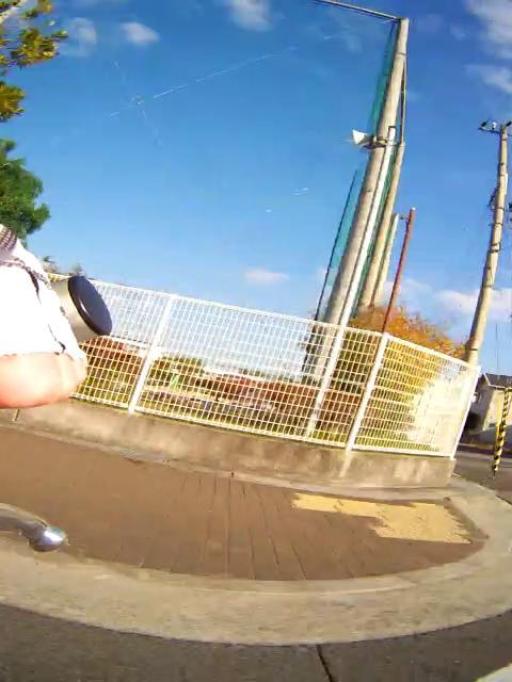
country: JP
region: Hyogo
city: Takarazuka
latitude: 34.7693
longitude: 135.3692
